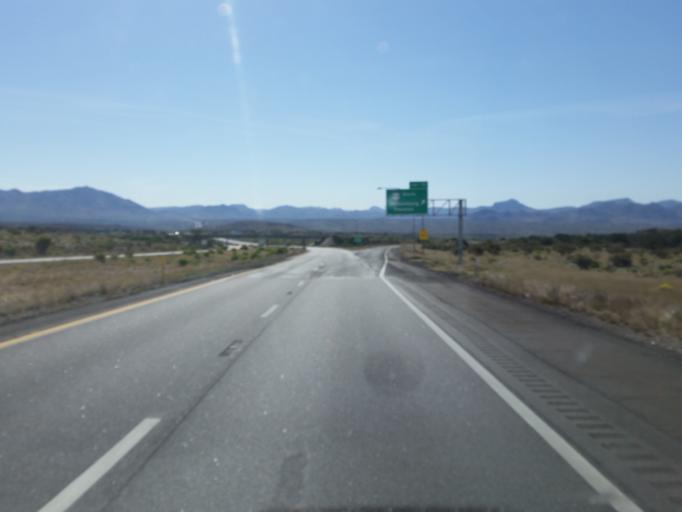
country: US
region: Arizona
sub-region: Mohave County
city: New Kingman-Butler
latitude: 35.1596
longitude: -113.7014
